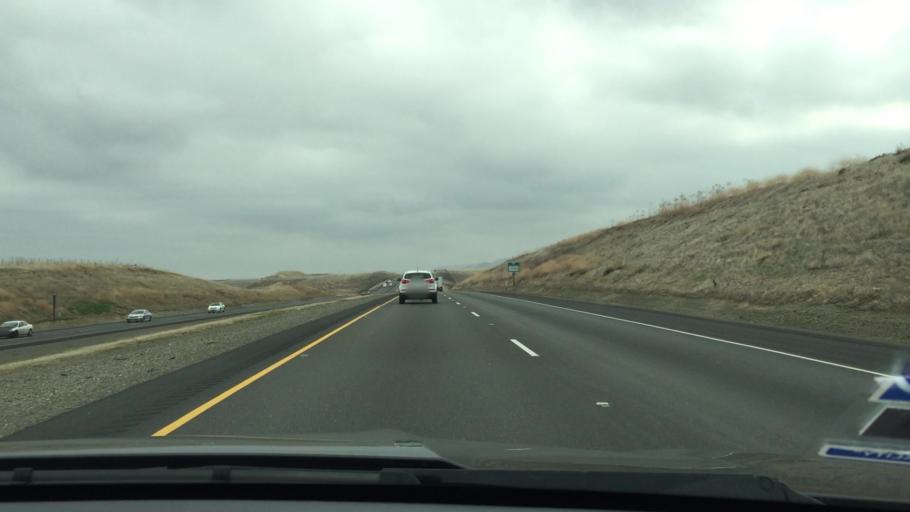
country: US
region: California
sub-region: Stanislaus County
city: Newman
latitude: 37.2766
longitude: -121.0969
